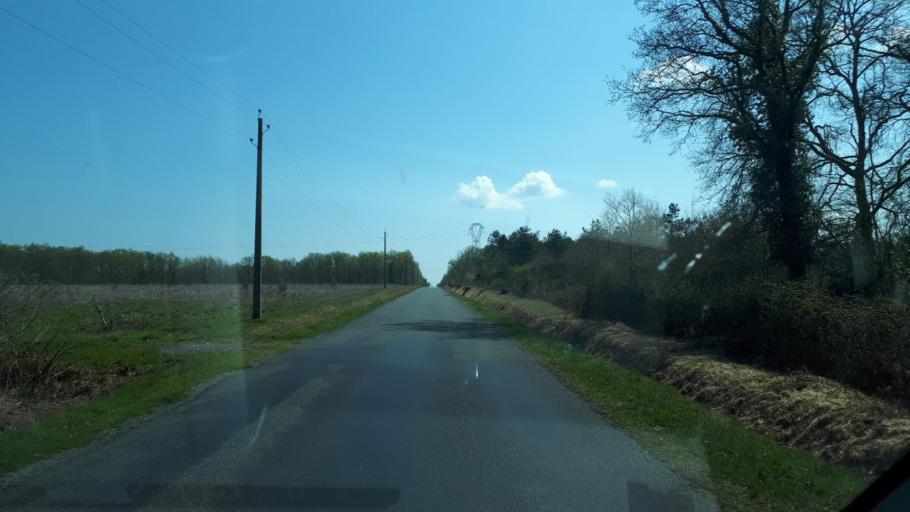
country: FR
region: Centre
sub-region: Departement du Cher
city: Neuvy-sur-Barangeon
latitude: 47.3201
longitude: 2.1931
